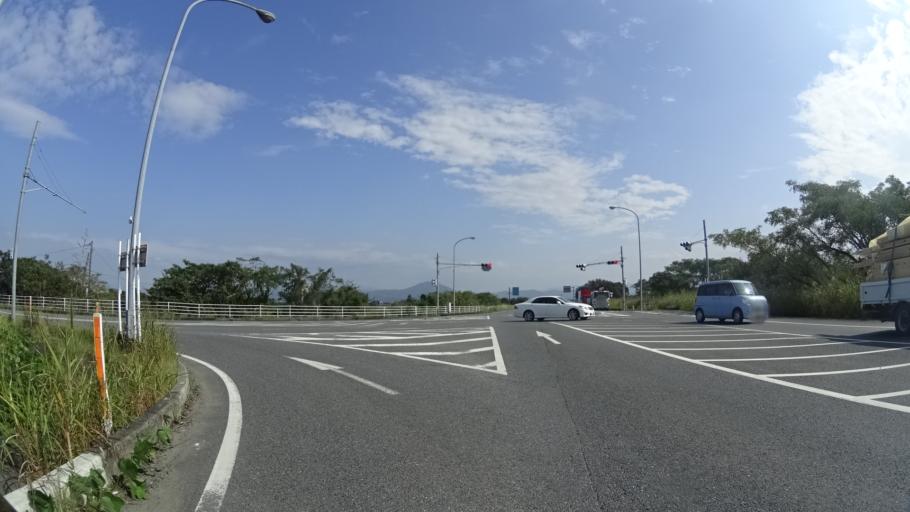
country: JP
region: Kumamoto
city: Kumamoto
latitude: 32.7354
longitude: 130.7501
